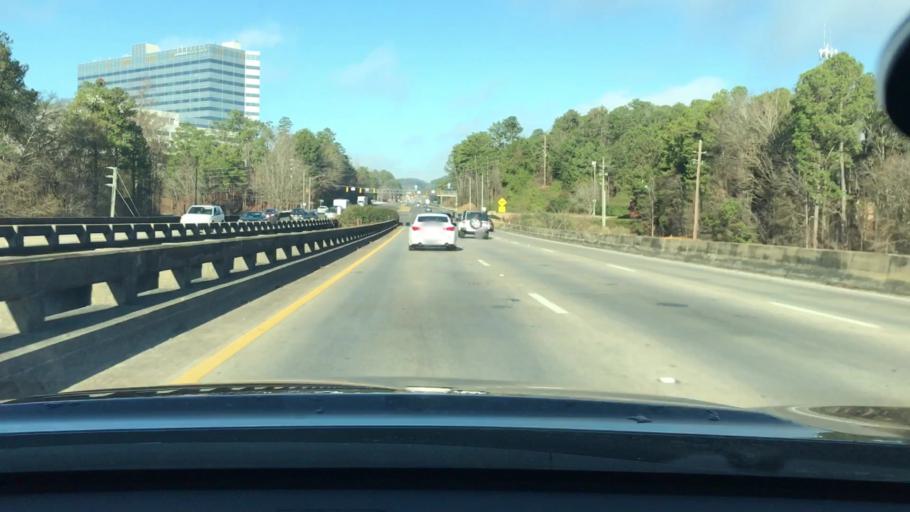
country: US
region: Alabama
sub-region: Shelby County
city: Lake Purdy
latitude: 33.4320
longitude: -86.7129
